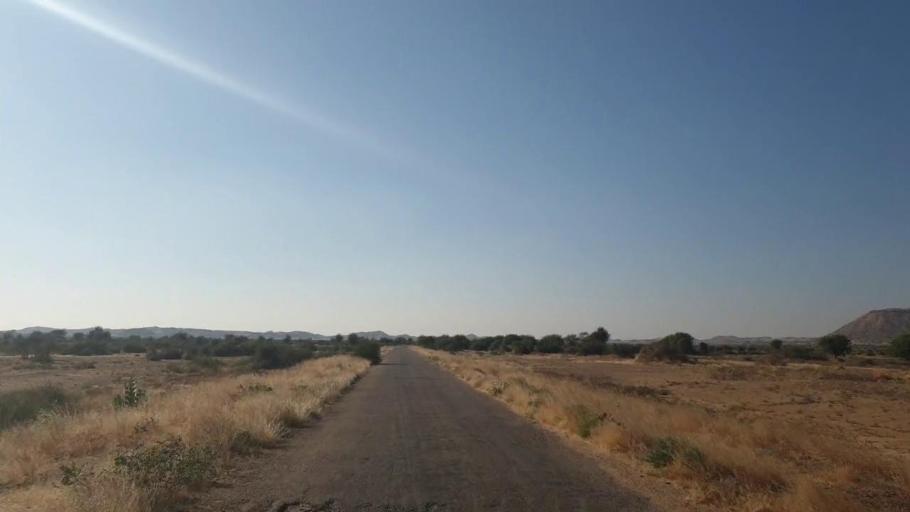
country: PK
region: Sindh
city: Malir Cantonment
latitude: 25.3894
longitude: 67.5197
